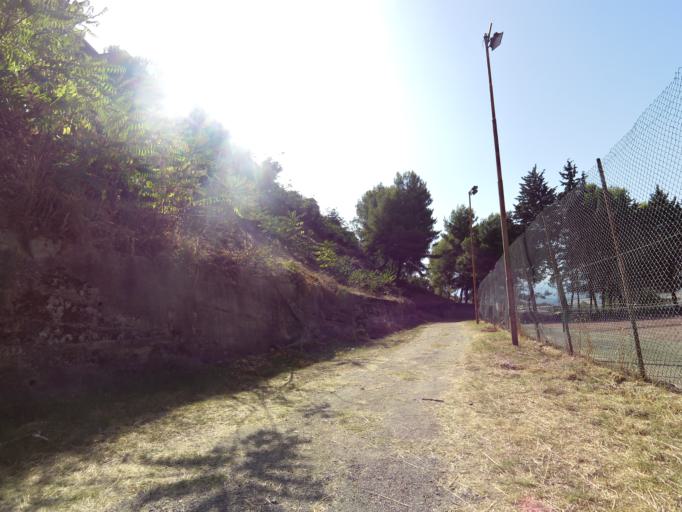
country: IT
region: Calabria
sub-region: Provincia di Reggio Calabria
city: Monasterace
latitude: 38.4537
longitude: 16.5545
